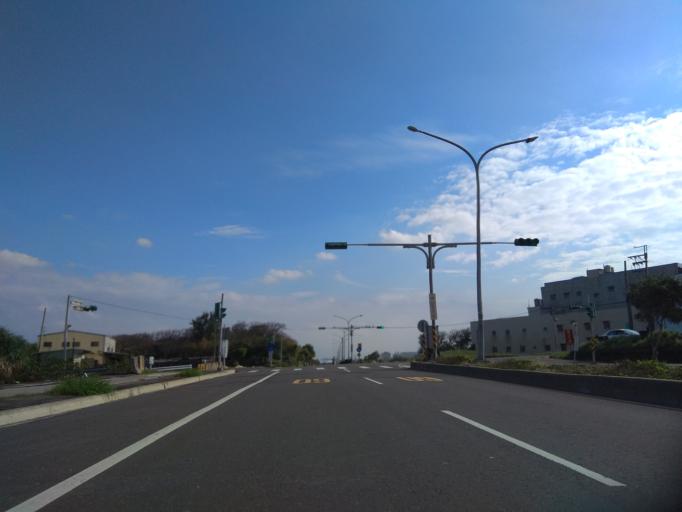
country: TW
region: Taiwan
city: Taoyuan City
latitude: 25.0780
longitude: 121.1698
